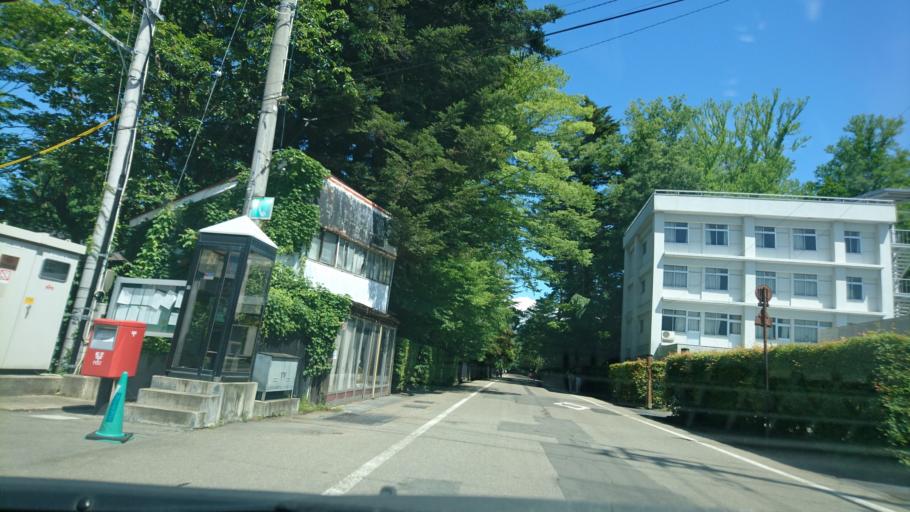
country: JP
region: Akita
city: Kakunodatemachi
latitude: 39.5965
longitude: 140.5623
